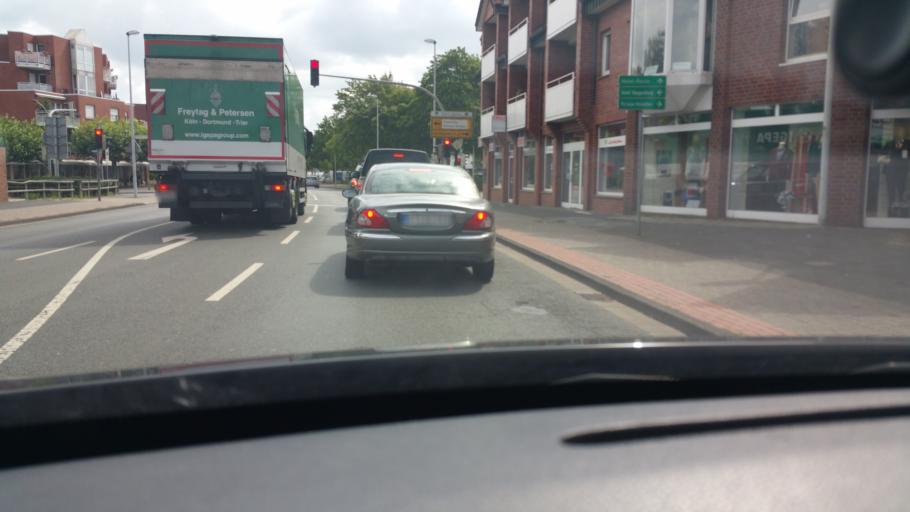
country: DE
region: North Rhine-Westphalia
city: Emsdetten
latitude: 52.1723
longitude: 7.5266
